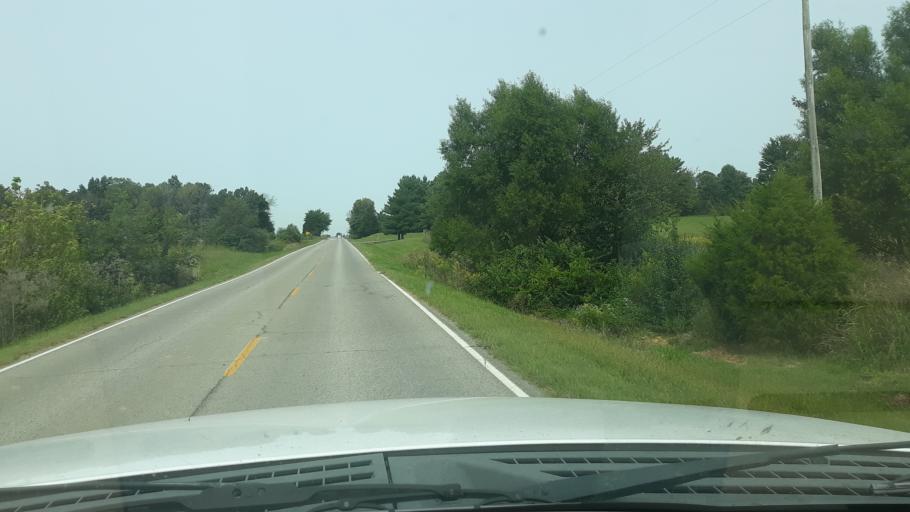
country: US
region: Illinois
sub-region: Saline County
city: Harrisburg
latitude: 37.8587
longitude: -88.6055
